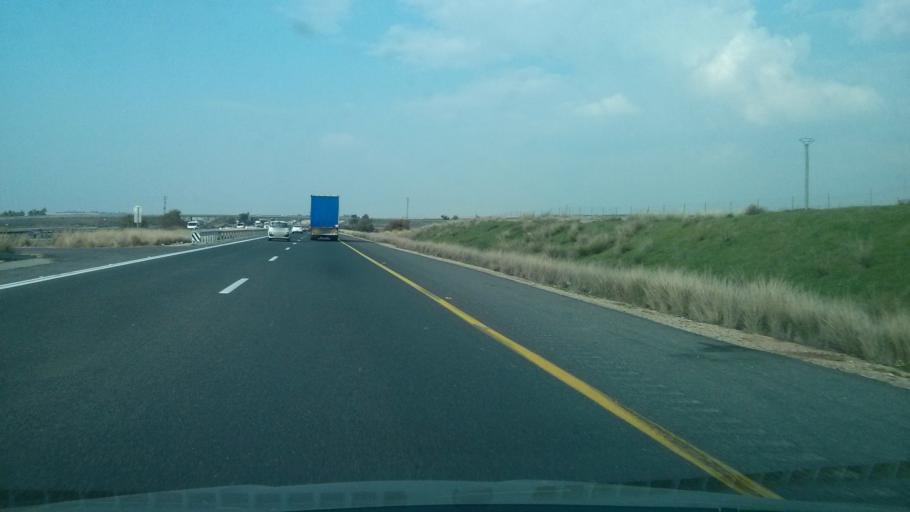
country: IL
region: Central District
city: Bene 'Ayish
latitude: 31.7396
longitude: 34.8226
